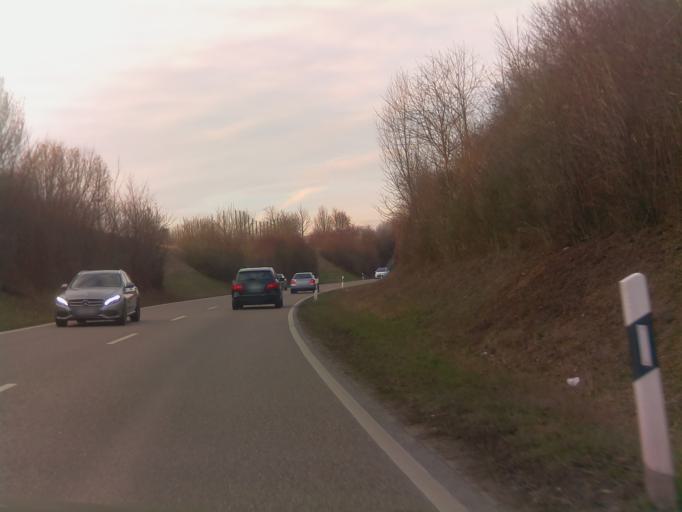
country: DE
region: Baden-Wuerttemberg
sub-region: Regierungsbezirk Stuttgart
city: Ditzingen
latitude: 48.8234
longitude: 9.0539
